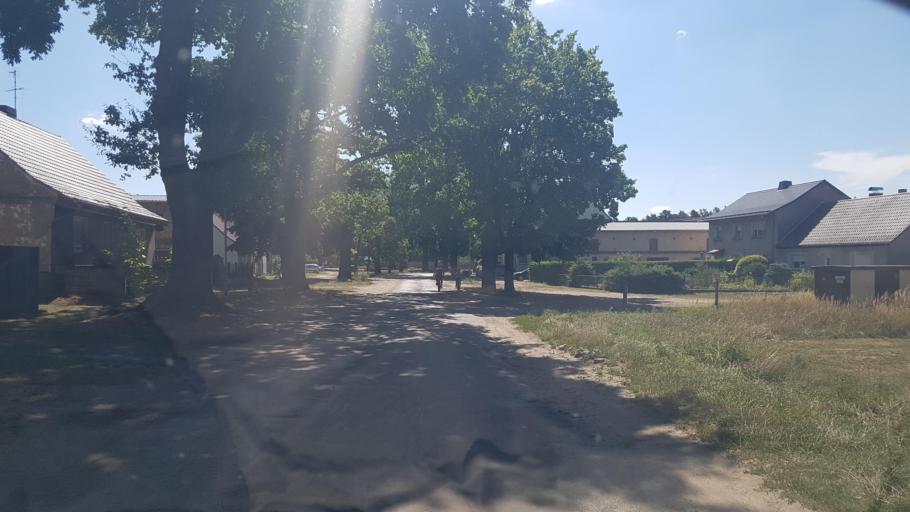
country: DE
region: Brandenburg
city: Golzow
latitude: 52.2953
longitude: 12.5857
